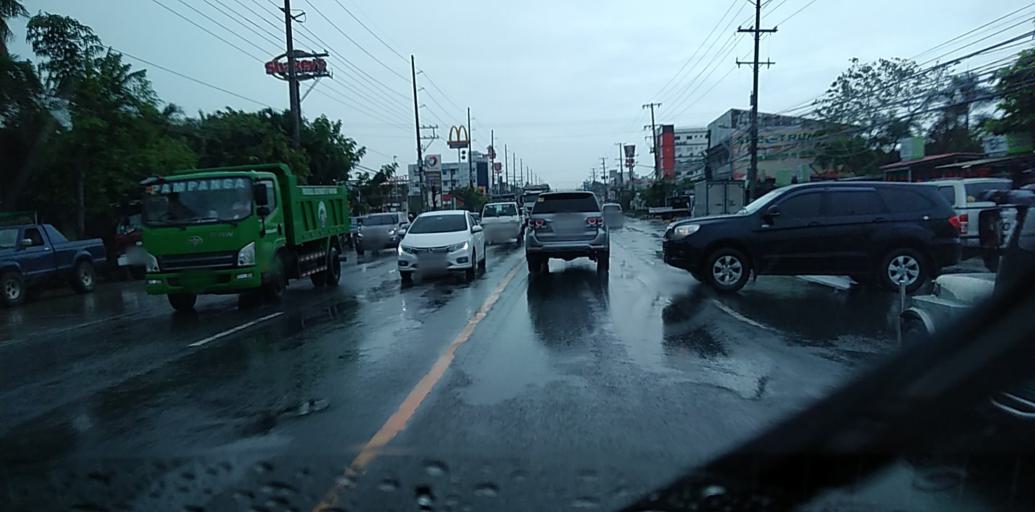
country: PH
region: Central Luzon
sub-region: Province of Pampanga
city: Bulaon
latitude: 15.0664
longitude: 120.6506
